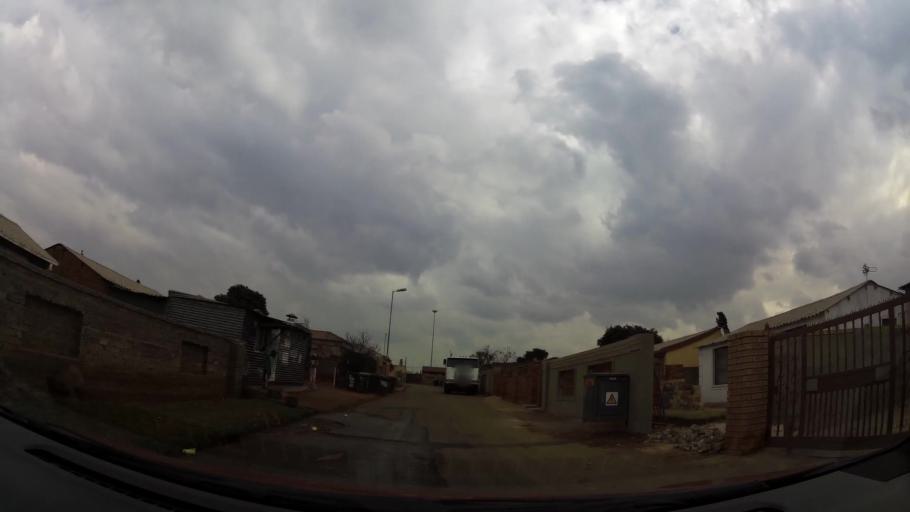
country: ZA
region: Gauteng
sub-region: City of Johannesburg Metropolitan Municipality
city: Soweto
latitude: -26.2604
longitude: 27.8364
